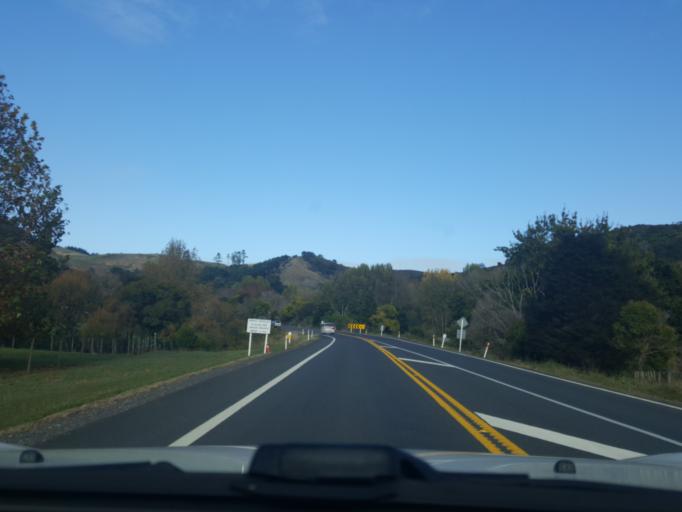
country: NZ
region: Waikato
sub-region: Hauraki District
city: Paeroa
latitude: -37.4080
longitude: 175.7065
